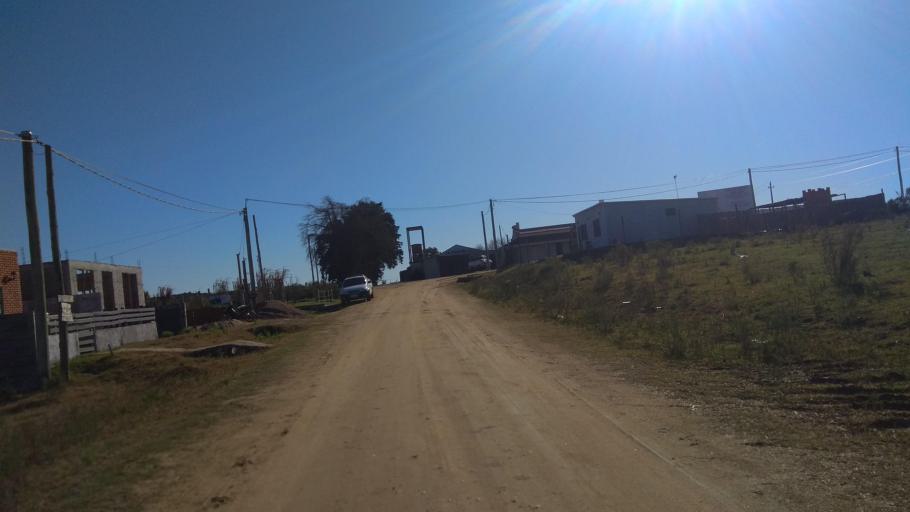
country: UY
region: Florida
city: Florida
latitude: -34.0837
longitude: -56.2396
